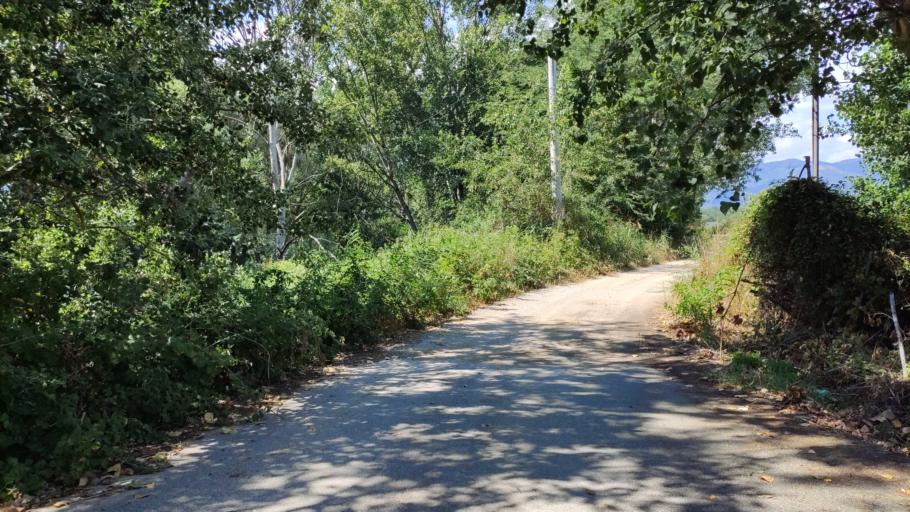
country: GR
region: East Macedonia and Thrace
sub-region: Nomos Rodopis
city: Komotini
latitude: 41.1114
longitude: 25.3709
